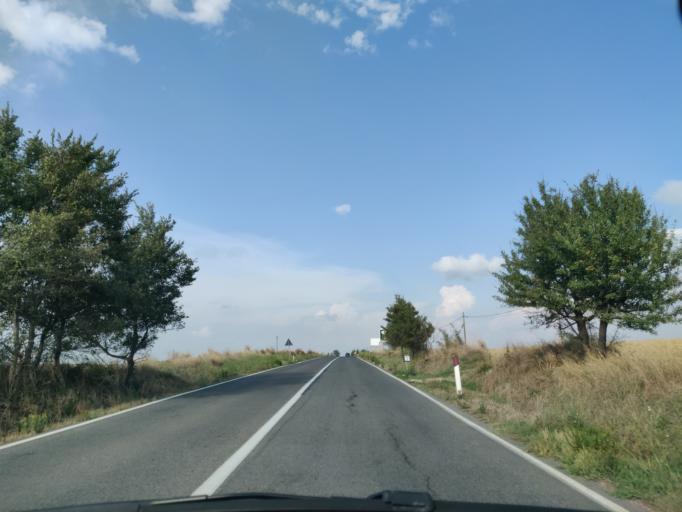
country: IT
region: Latium
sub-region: Provincia di Viterbo
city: Tarquinia
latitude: 42.2412
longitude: 11.8060
